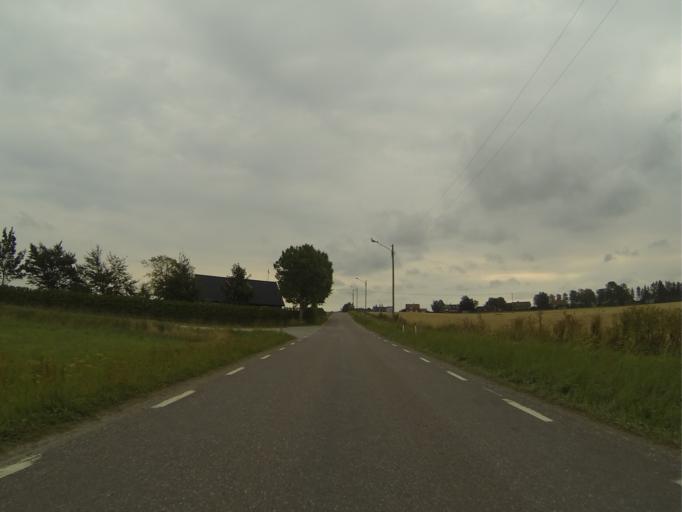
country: SE
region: Skane
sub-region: Lunds Kommun
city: Lund
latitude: 55.7425
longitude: 13.2749
